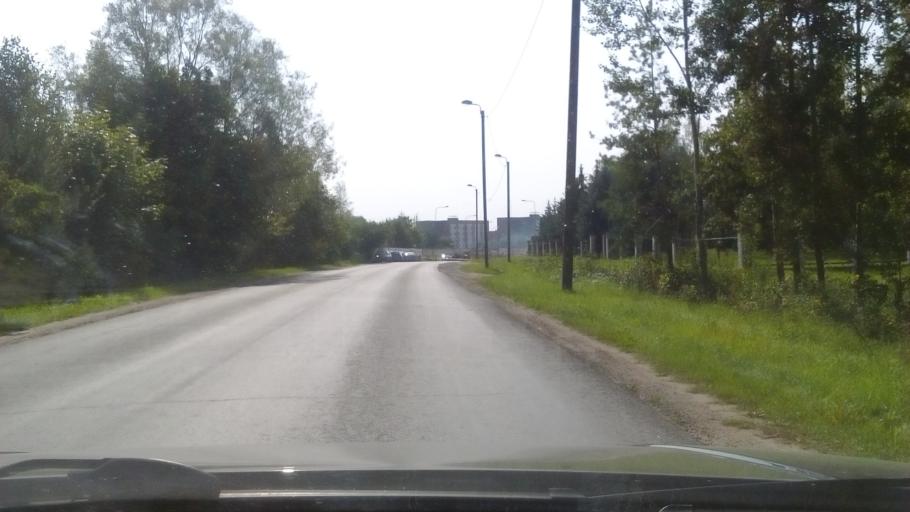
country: LT
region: Alytaus apskritis
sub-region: Alytus
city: Alytus
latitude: 54.4273
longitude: 24.0346
